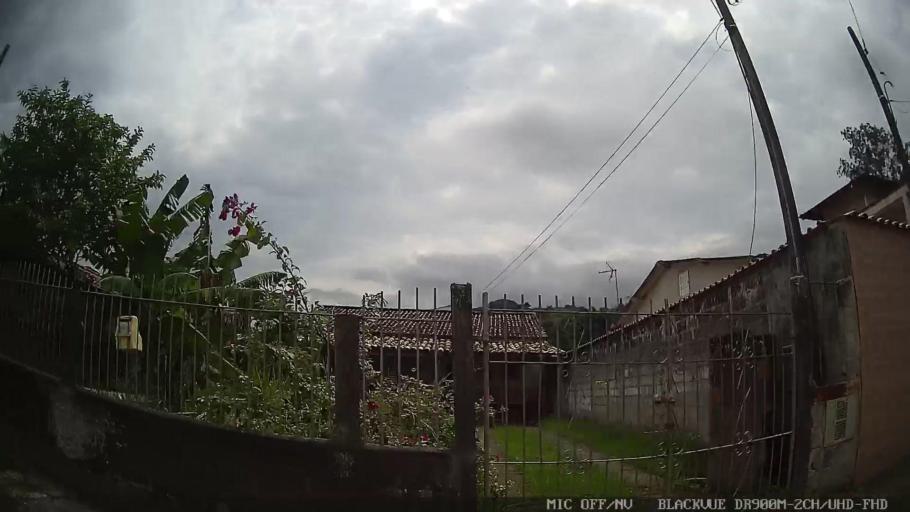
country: BR
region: Sao Paulo
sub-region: Caraguatatuba
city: Caraguatatuba
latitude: -23.6181
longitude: -45.4166
